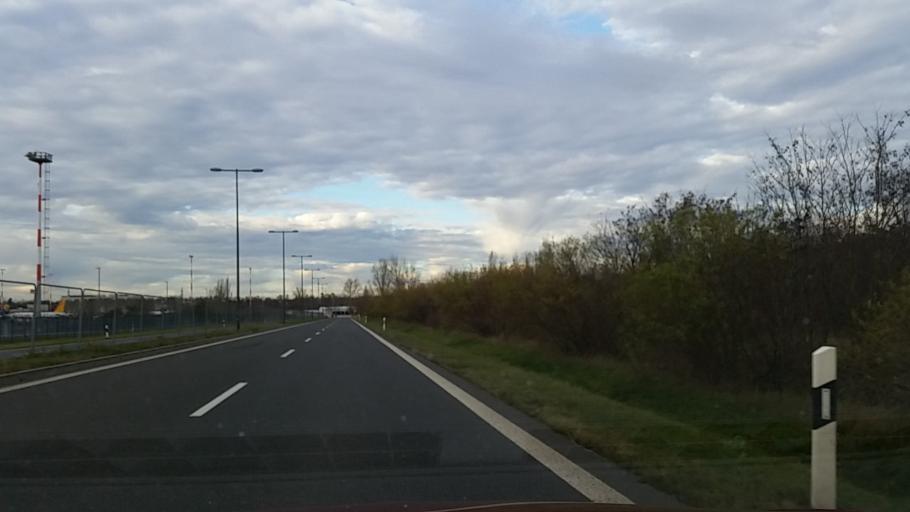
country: DE
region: Brandenburg
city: Schonefeld
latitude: 52.3872
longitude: 13.5266
